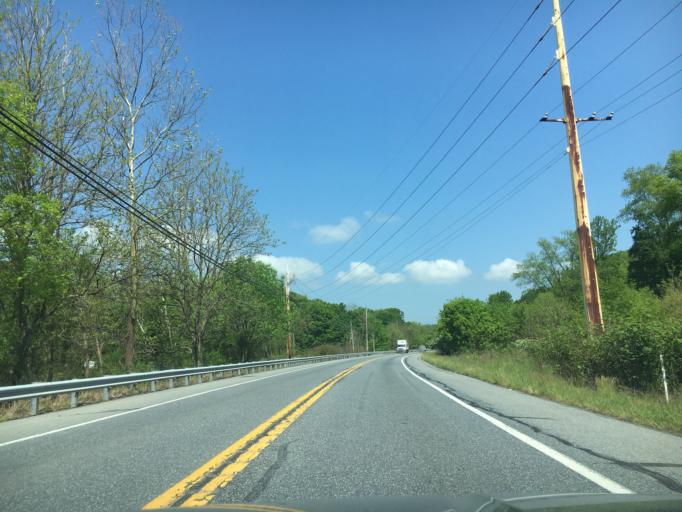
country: US
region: Pennsylvania
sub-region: Berks County
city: Boyertown
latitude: 40.3382
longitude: -75.6567
